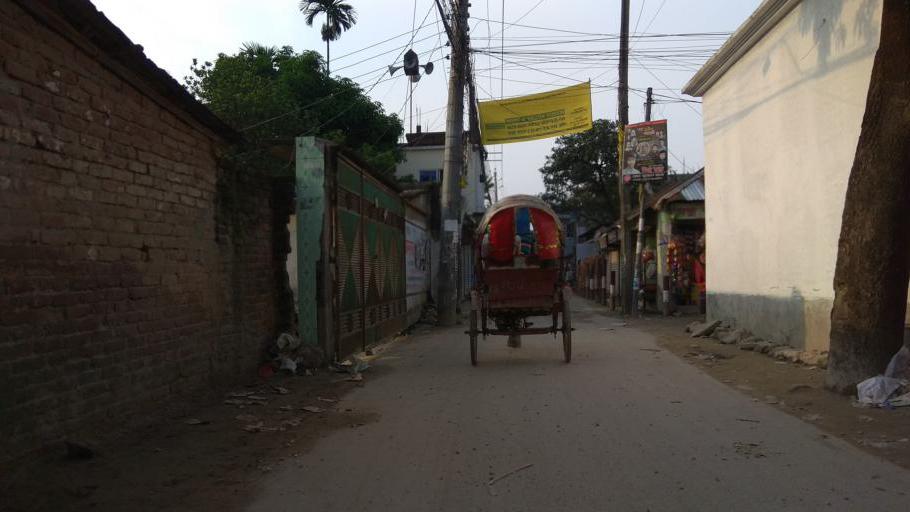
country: BD
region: Dhaka
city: Tungi
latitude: 23.8429
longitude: 90.3873
